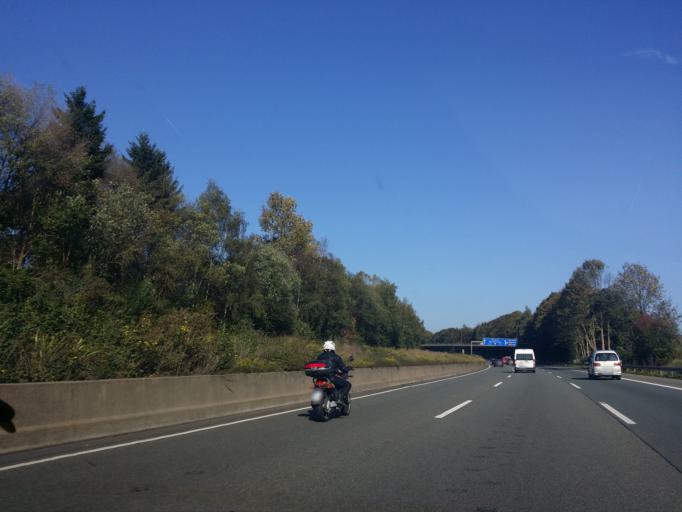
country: DE
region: North Rhine-Westphalia
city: Burscheid
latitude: 51.0776
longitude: 7.1241
